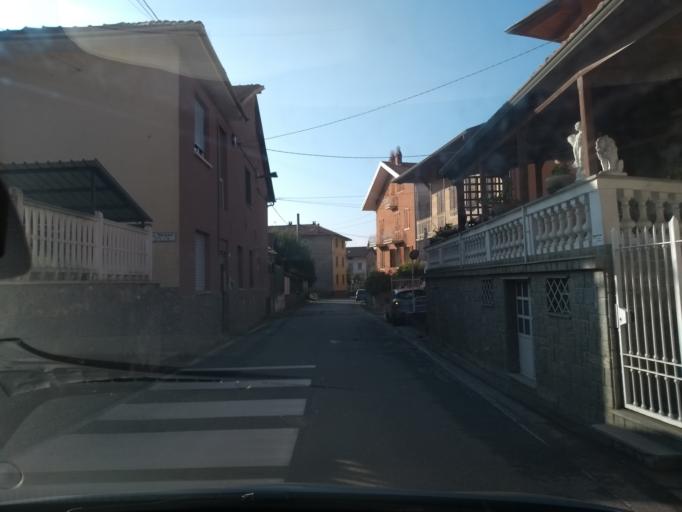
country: IT
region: Piedmont
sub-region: Provincia di Torino
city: Monasterolo
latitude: 45.2347
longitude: 7.5081
